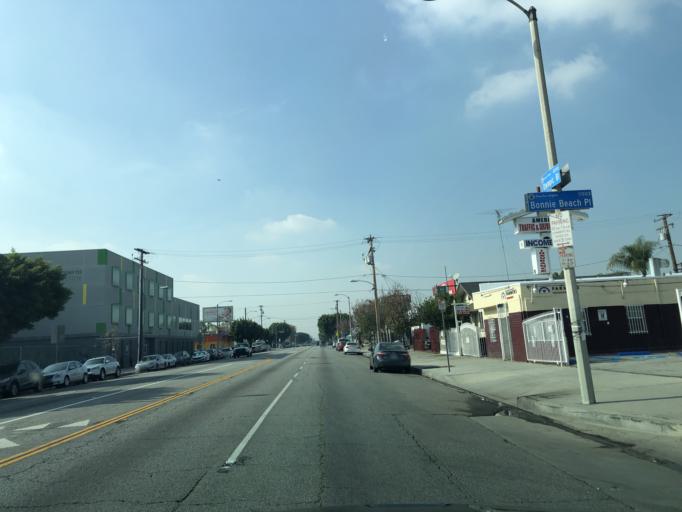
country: US
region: California
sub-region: Los Angeles County
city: East Los Angeles
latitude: 34.0190
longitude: -118.1812
